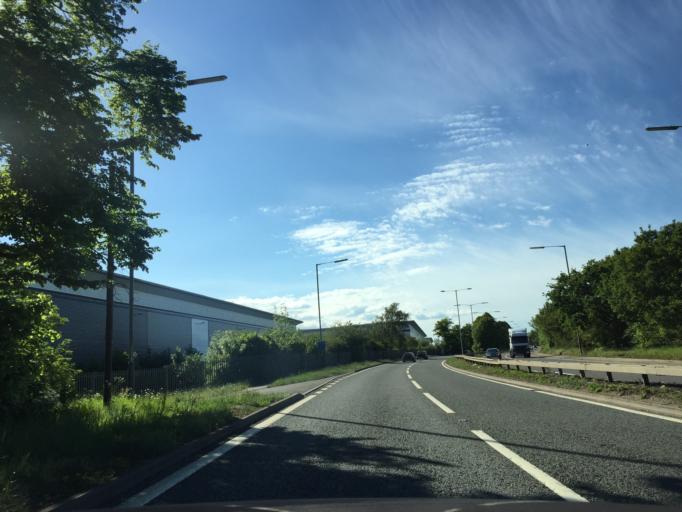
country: GB
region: England
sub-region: Warwickshire
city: Ryton on Dunsmore
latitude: 52.3673
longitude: -1.4408
